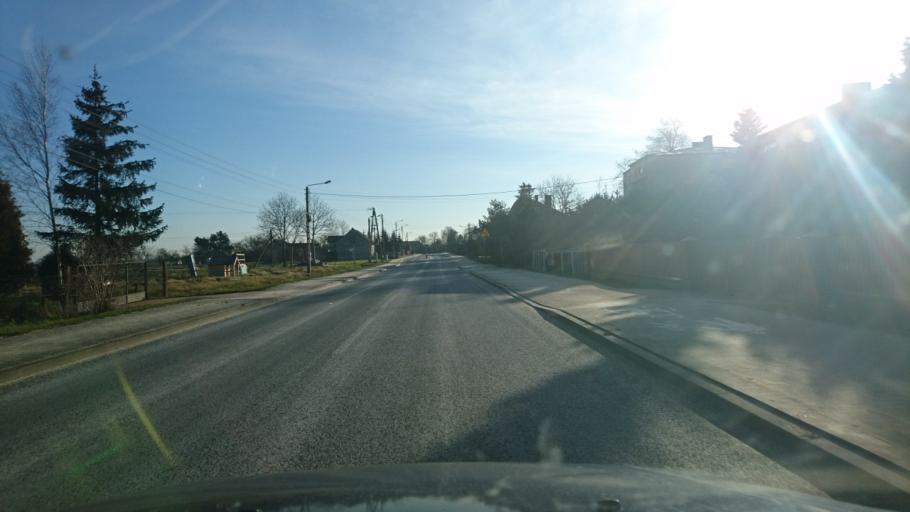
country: PL
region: Silesian Voivodeship
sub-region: Powiat klobucki
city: Starokrzepice
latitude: 51.0078
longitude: 18.6581
